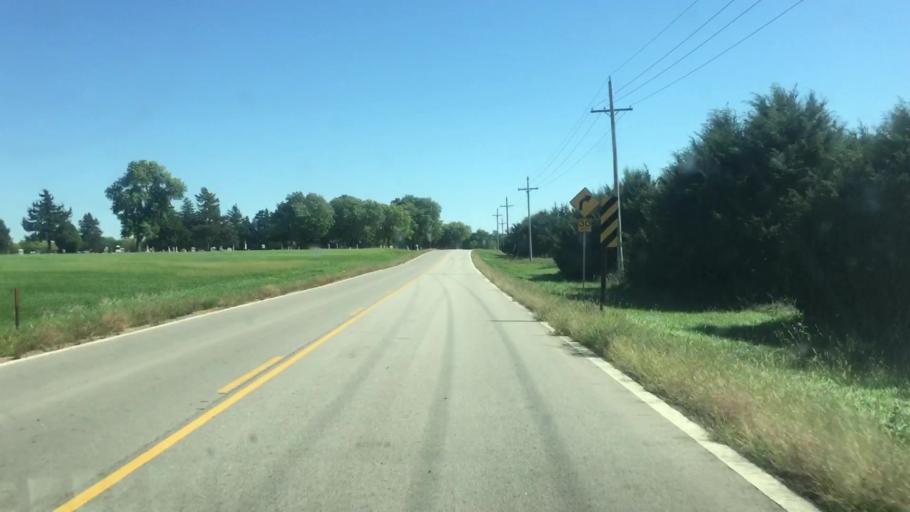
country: US
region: Kansas
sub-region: Jackson County
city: Holton
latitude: 39.6097
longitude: -95.7254
